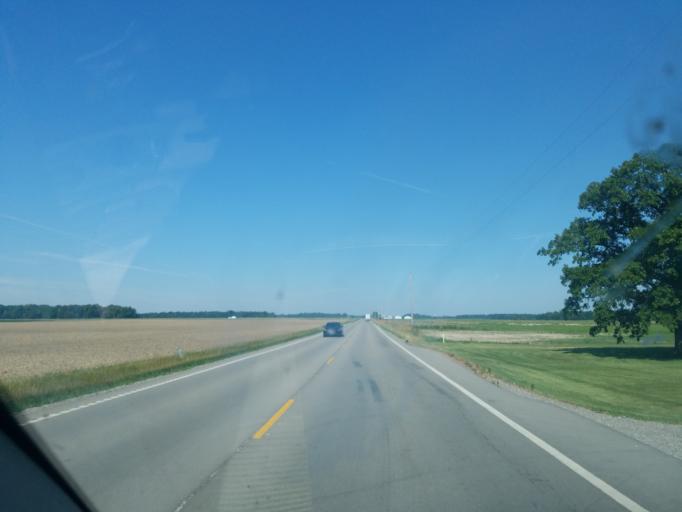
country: US
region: Ohio
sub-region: Shelby County
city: Jackson Center
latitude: 40.4393
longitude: -83.9756
